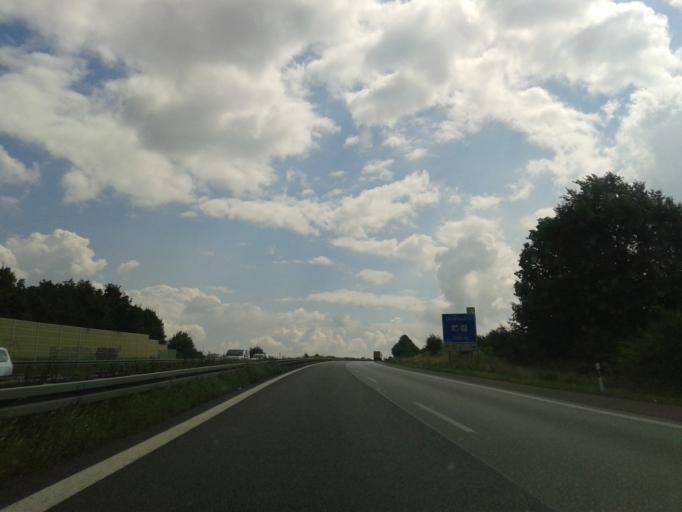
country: DE
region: Saxony
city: Goda
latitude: 51.2034
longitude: 14.3080
